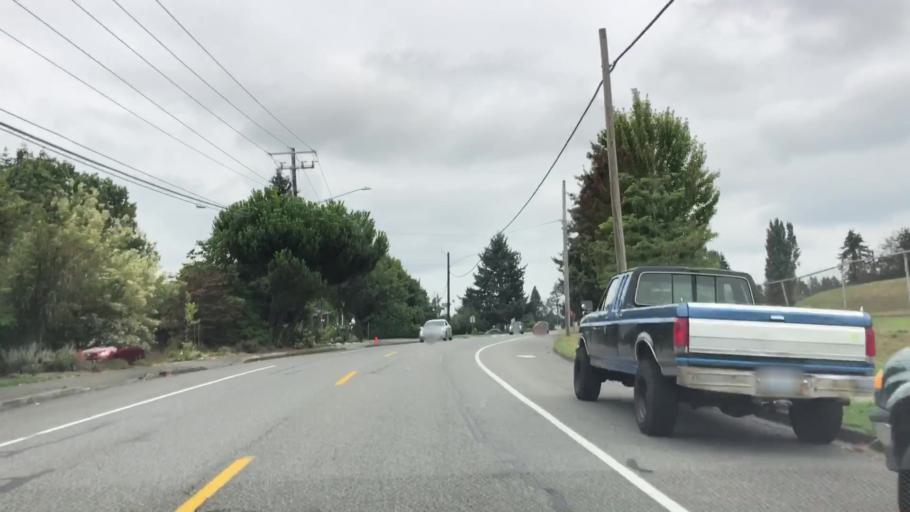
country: US
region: Washington
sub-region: Snohomish County
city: Snohomish
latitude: 47.9263
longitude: -122.0854
